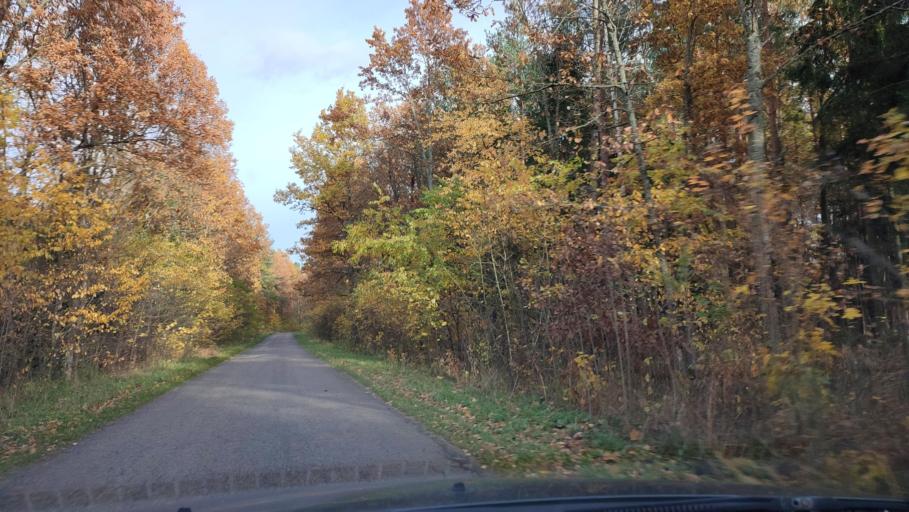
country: PL
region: Warmian-Masurian Voivodeship
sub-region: Powiat szczycienski
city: Szczytno
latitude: 53.5270
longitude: 20.9173
